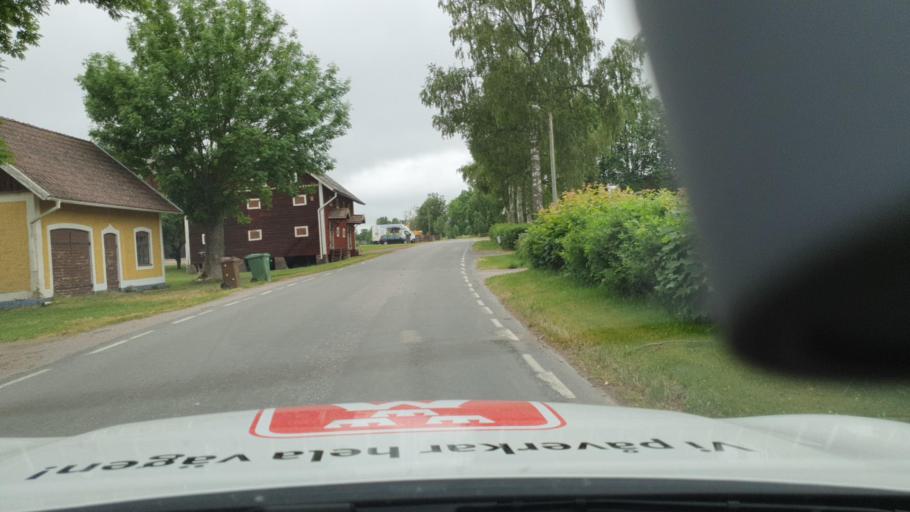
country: SE
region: Vaestra Goetaland
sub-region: Tidaholms Kommun
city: Olofstorp
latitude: 58.3650
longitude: 14.0493
